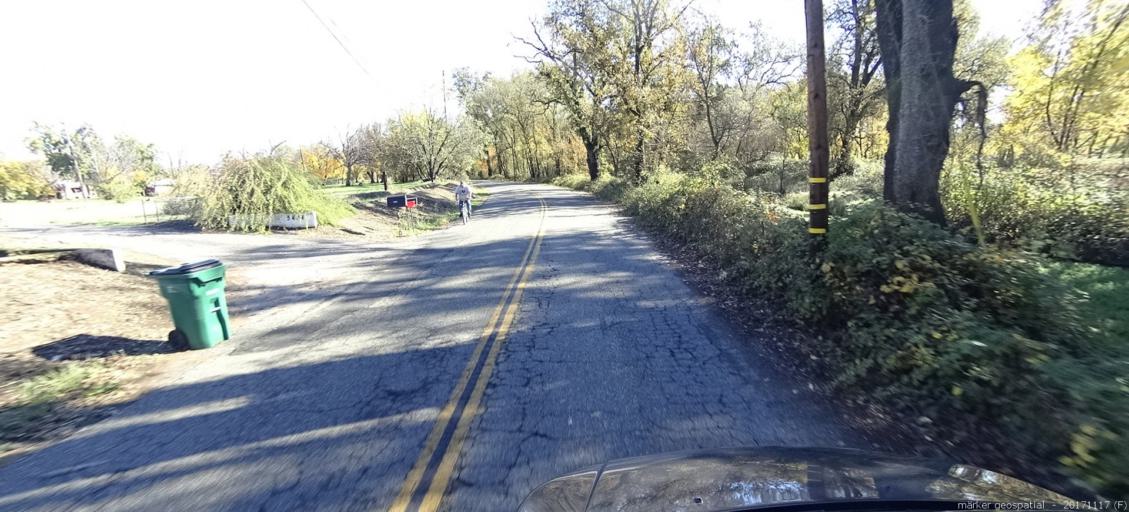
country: US
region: California
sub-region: Shasta County
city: Anderson
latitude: 40.4456
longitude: -122.2468
